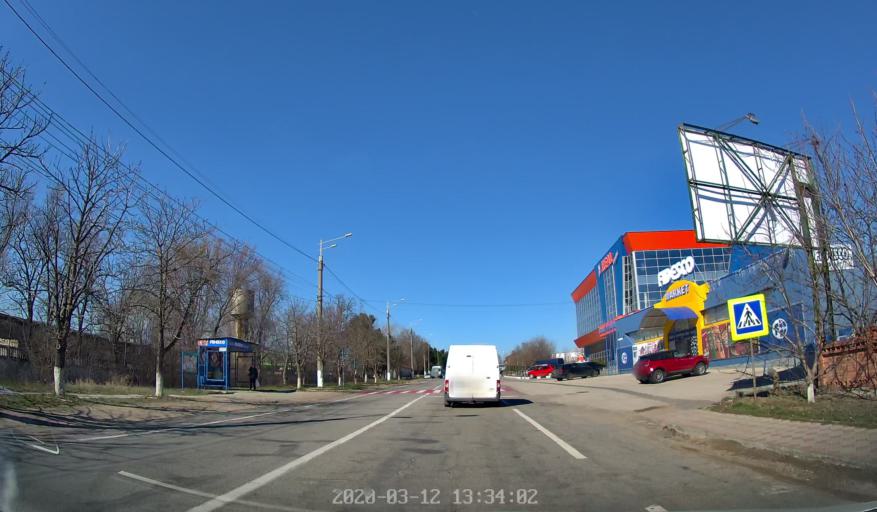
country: MD
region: Laloveni
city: Ialoveni
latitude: 46.9607
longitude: 28.7678
